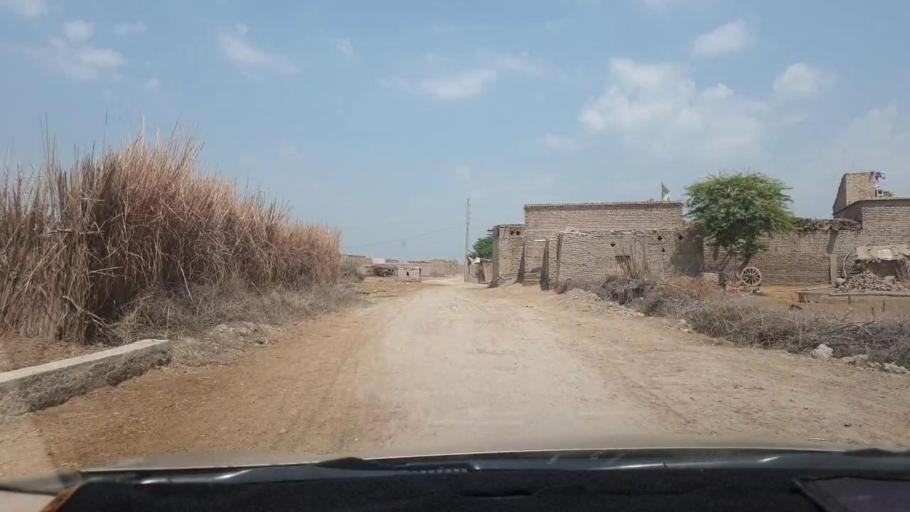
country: PK
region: Sindh
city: Naudero
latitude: 27.7335
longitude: 68.3264
